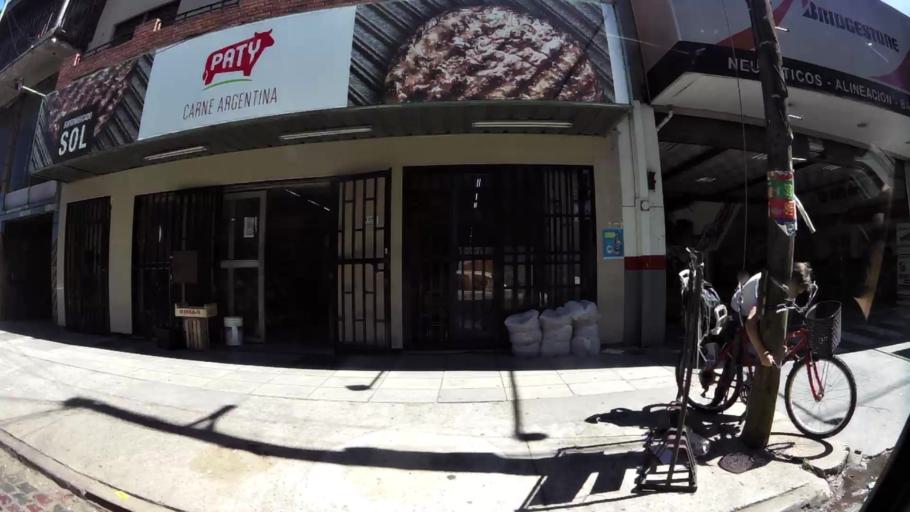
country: AR
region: Buenos Aires
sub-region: Partido de Vicente Lopez
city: Olivos
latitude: -34.5231
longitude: -58.5098
